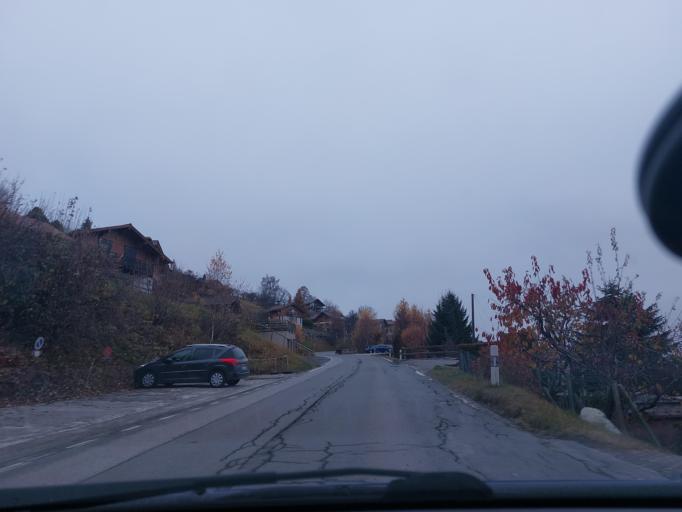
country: CH
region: Valais
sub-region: Conthey District
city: Basse-Nendaz
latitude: 46.1845
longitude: 7.3064
